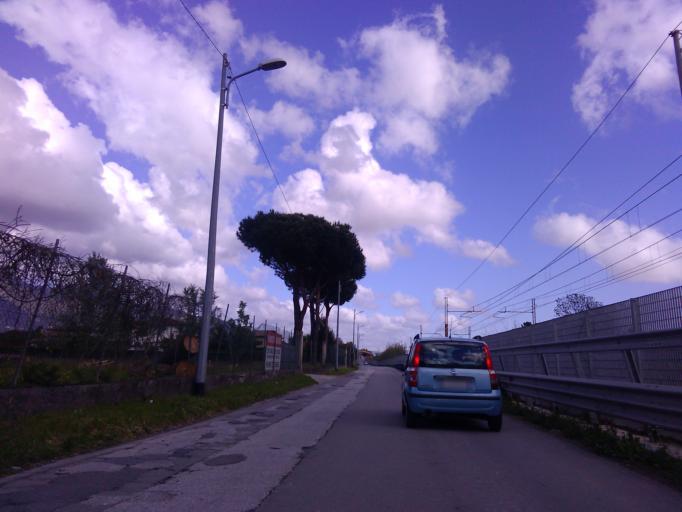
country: IT
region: Tuscany
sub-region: Provincia di Lucca
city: Strettoia
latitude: 43.9885
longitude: 10.1849
